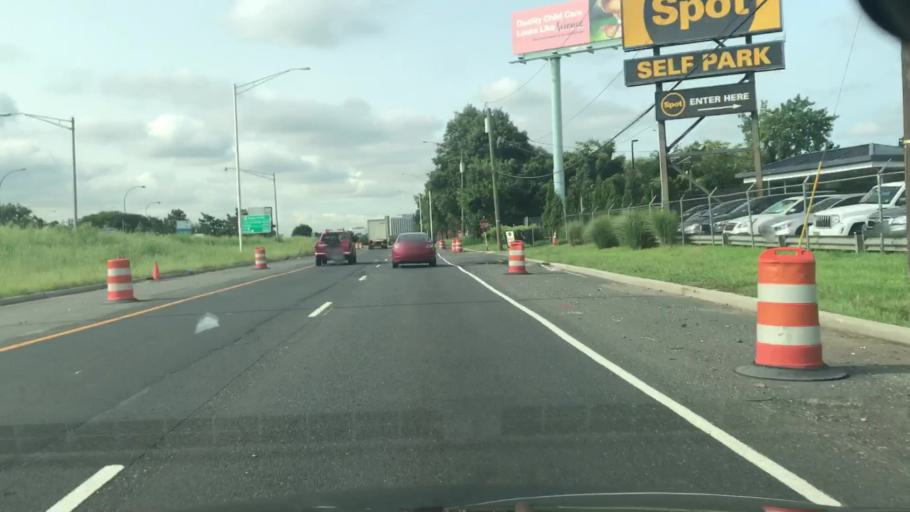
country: US
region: New Jersey
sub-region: Union County
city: Elizabeth
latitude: 40.6970
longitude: -74.1881
